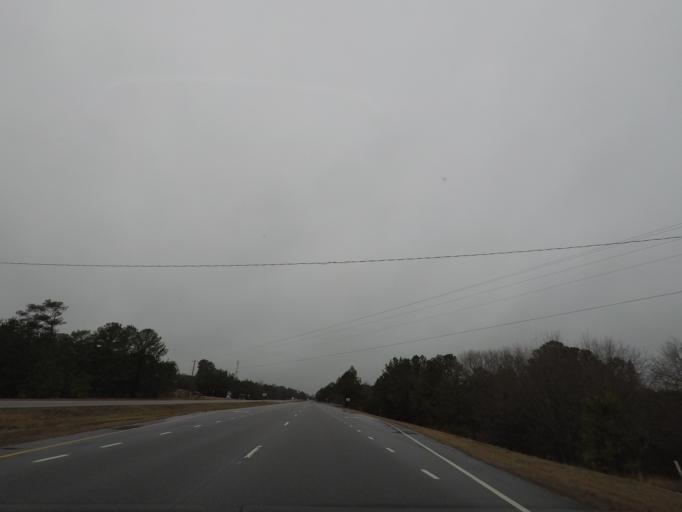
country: US
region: North Carolina
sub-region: Lee County
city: Broadway
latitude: 35.3375
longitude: -79.0974
